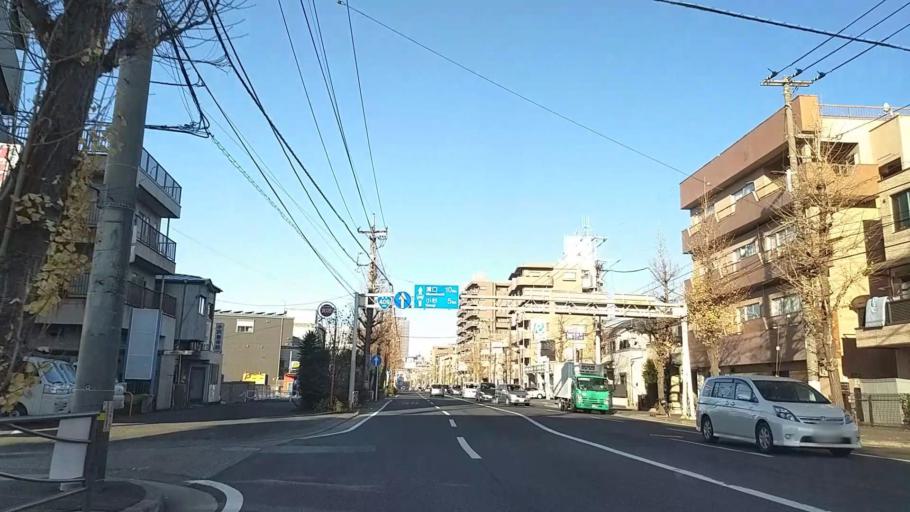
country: JP
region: Kanagawa
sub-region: Kawasaki-shi
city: Kawasaki
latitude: 35.5442
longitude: 139.6907
